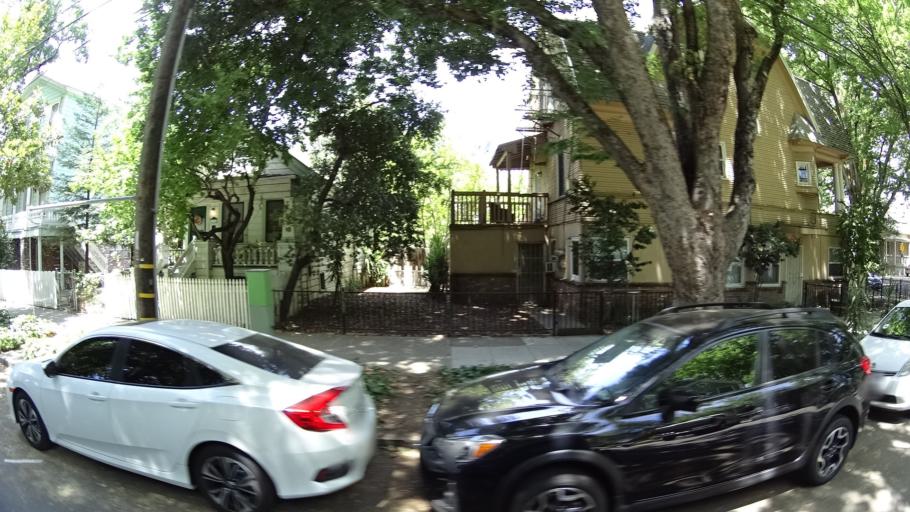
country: US
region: California
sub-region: Sacramento County
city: Sacramento
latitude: 38.5830
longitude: -121.4861
